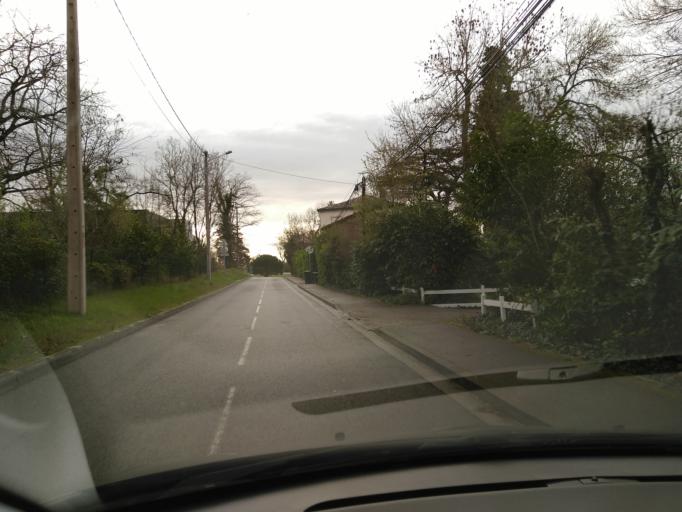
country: FR
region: Midi-Pyrenees
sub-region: Departement de la Haute-Garonne
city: Rouffiac-Tolosan
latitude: 43.6707
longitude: 1.5136
